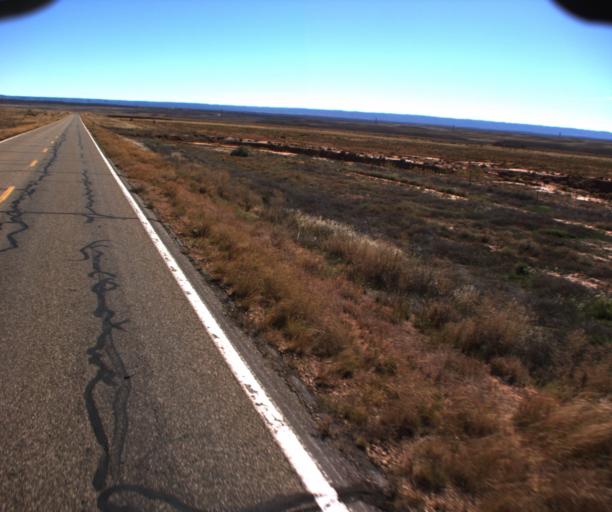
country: US
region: Arizona
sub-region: Coconino County
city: Fredonia
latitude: 36.9240
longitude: -112.4568
